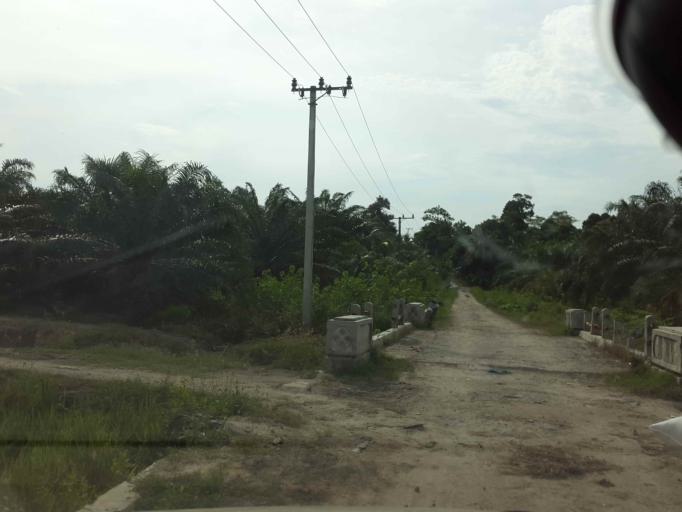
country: ID
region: Lampung
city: Palas
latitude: -5.6355
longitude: 105.7120
